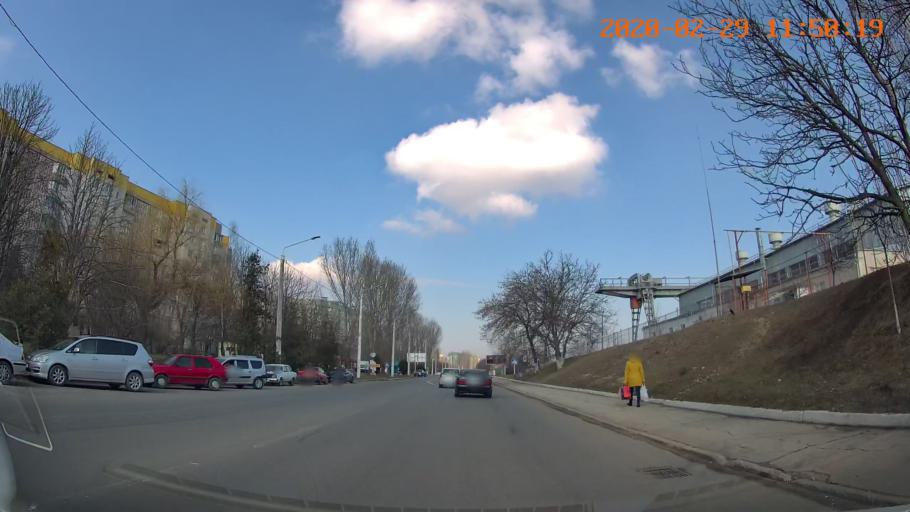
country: MD
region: Telenesti
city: Ribnita
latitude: 47.7572
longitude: 28.9910
